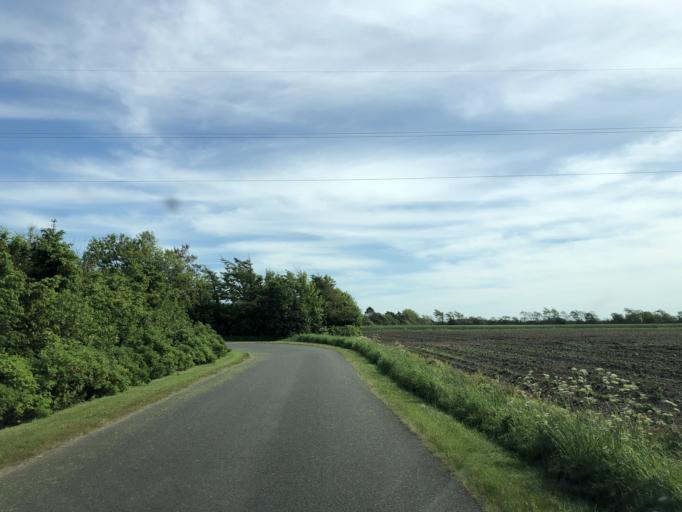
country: DK
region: Central Jutland
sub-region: Holstebro Kommune
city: Ulfborg
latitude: 56.2799
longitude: 8.2661
